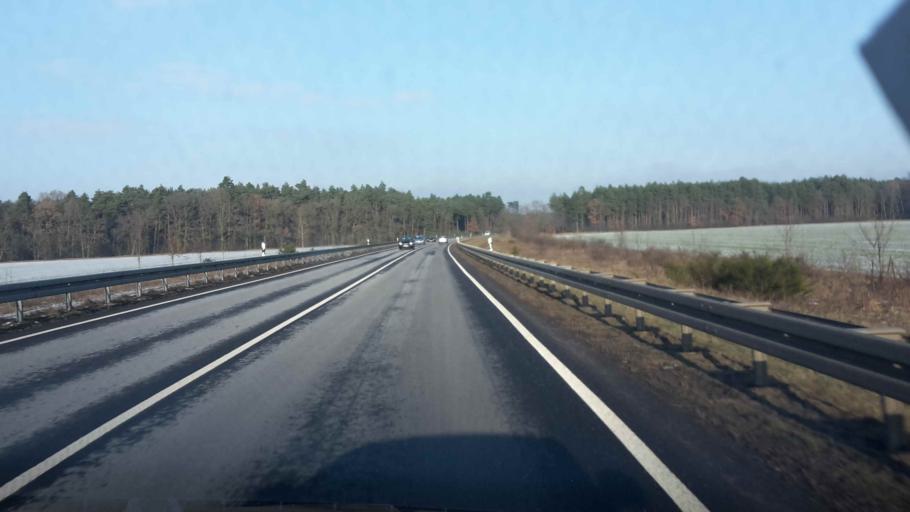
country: DE
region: Brandenburg
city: Weisen
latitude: 53.0265
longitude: 11.7741
